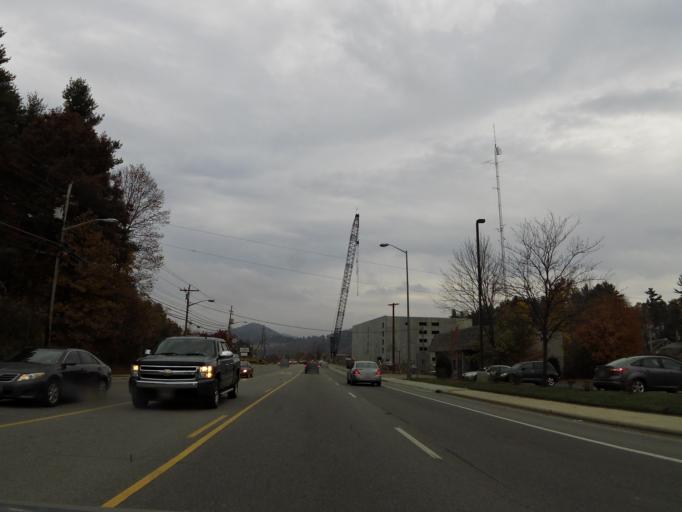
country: US
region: North Carolina
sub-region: Watauga County
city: Boone
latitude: 36.2086
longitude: -81.6731
